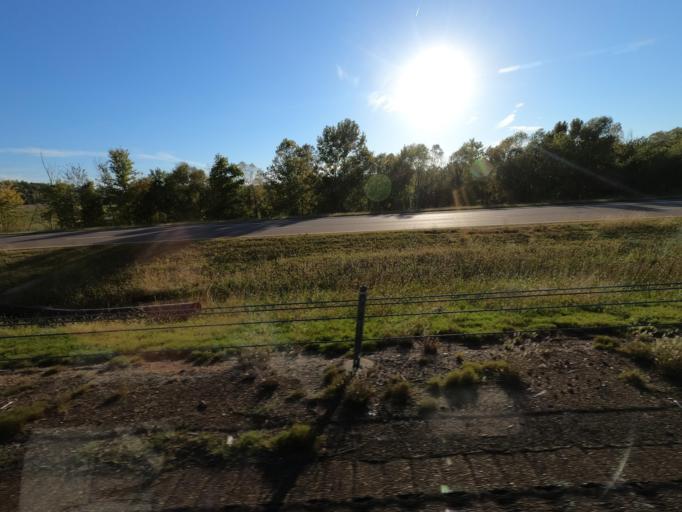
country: US
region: Tennessee
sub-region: Shelby County
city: Arlington
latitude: 35.2913
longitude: -89.6889
